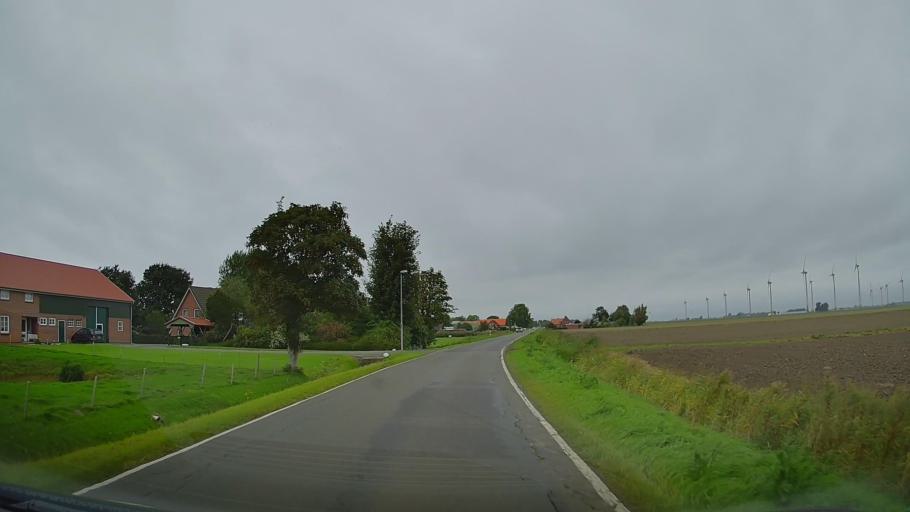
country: DE
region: Schleswig-Holstein
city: Neufeld
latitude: 53.9093
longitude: 9.0080
